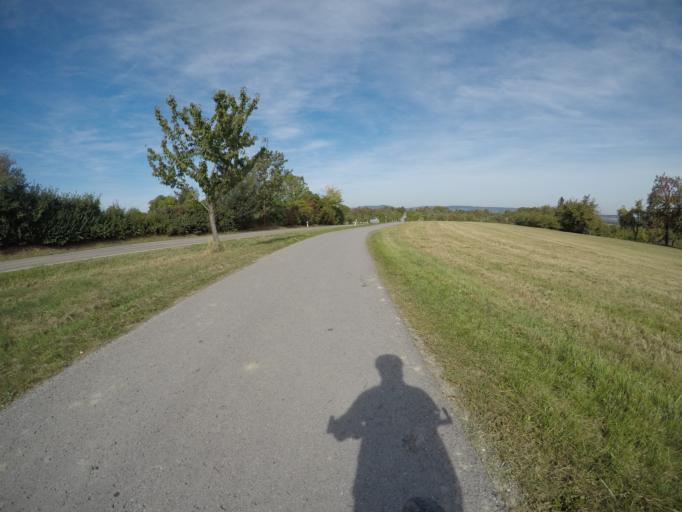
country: DE
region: Baden-Wuerttemberg
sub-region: Regierungsbezirk Stuttgart
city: Markgroningen
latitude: 48.9187
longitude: 9.0738
